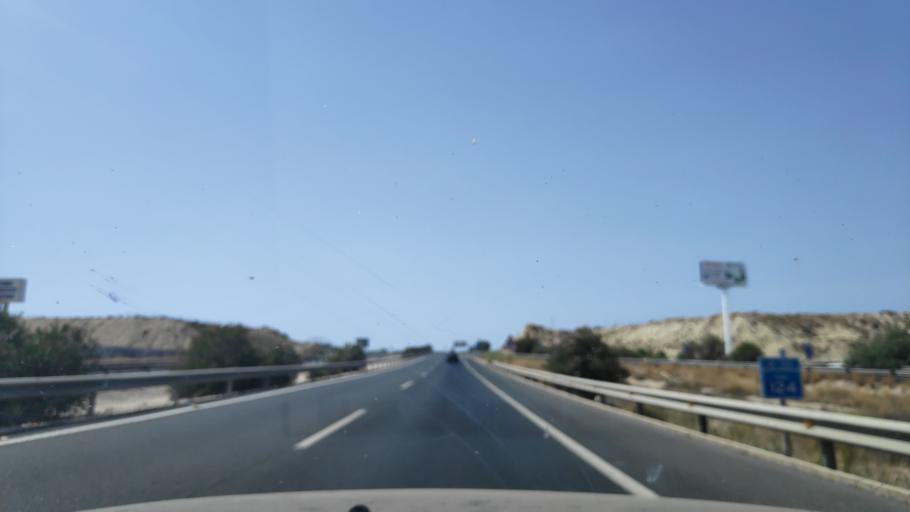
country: ES
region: Murcia
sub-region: Murcia
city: Lorqui
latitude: 38.1032
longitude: -1.2345
